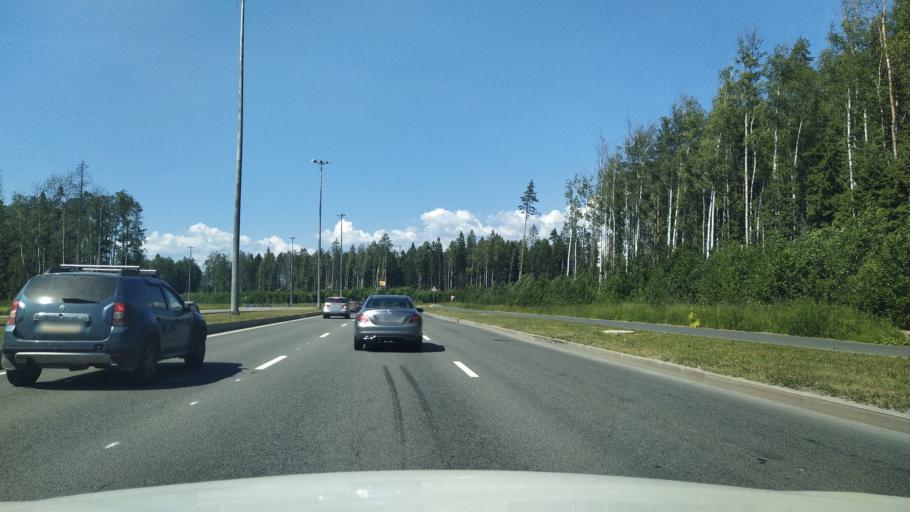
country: RU
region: St.-Petersburg
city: Levashovo
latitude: 60.0619
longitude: 30.2164
